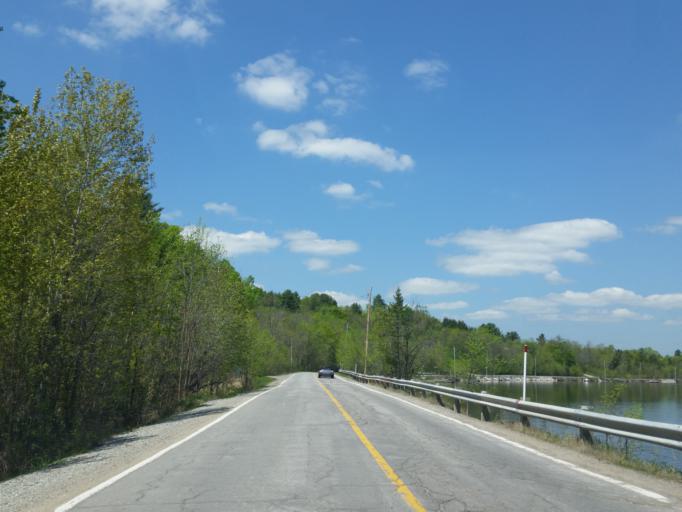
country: CA
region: Quebec
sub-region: Outaouais
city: Wakefield
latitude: 45.5951
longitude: -75.8788
